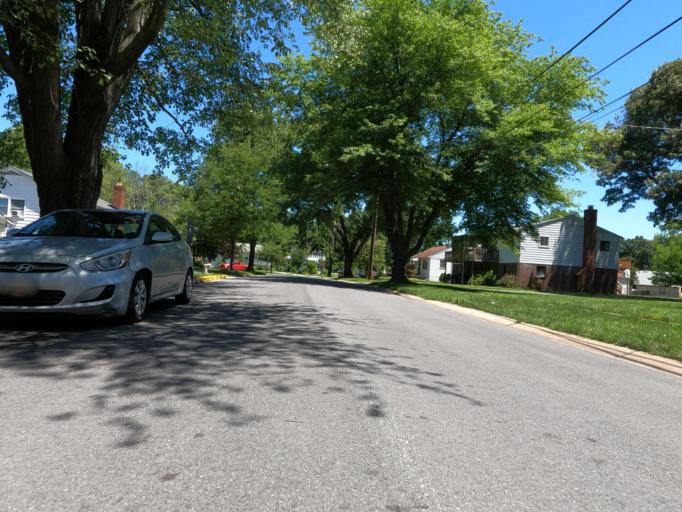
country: US
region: Maryland
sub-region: Prince George's County
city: College Park
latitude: 38.9897
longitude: -76.9260
